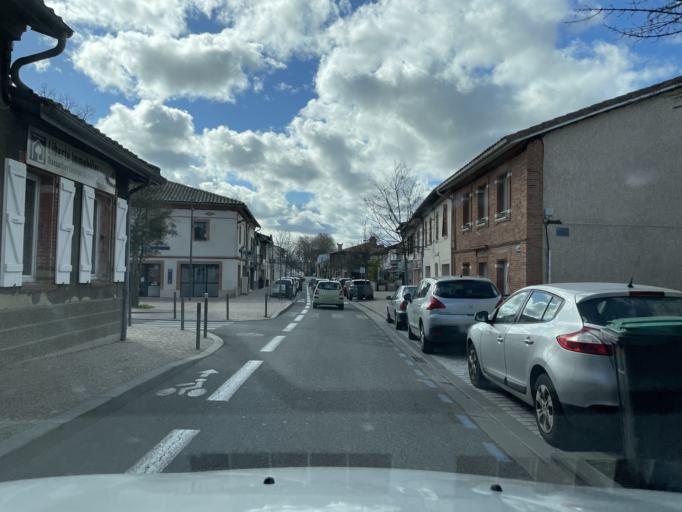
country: FR
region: Midi-Pyrenees
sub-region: Departement de la Haute-Garonne
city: Leguevin
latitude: 43.6000
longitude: 1.2339
